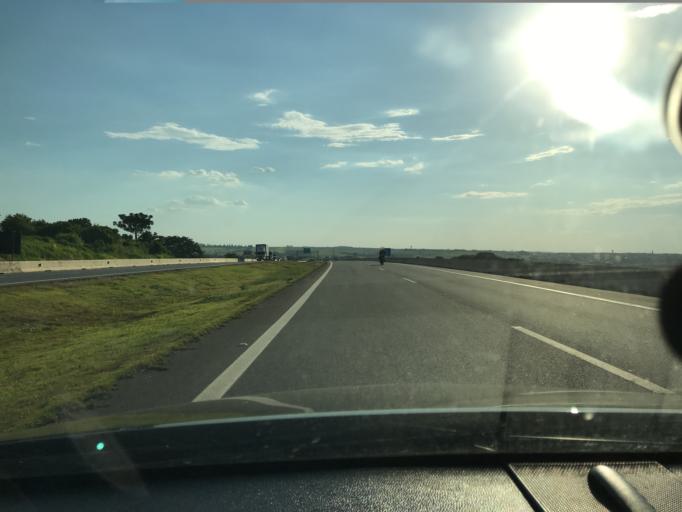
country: BR
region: Sao Paulo
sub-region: Valinhos
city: Valinhos
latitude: -22.9929
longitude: -47.0711
